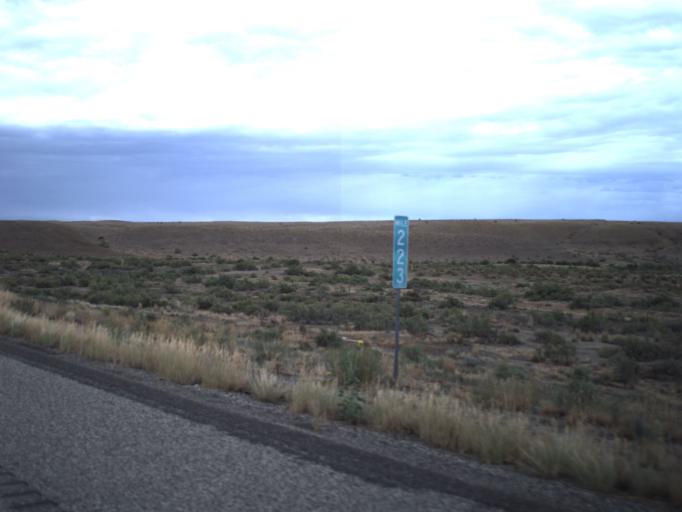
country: US
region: Colorado
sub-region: Mesa County
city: Loma
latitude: 39.1243
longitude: -109.1684
